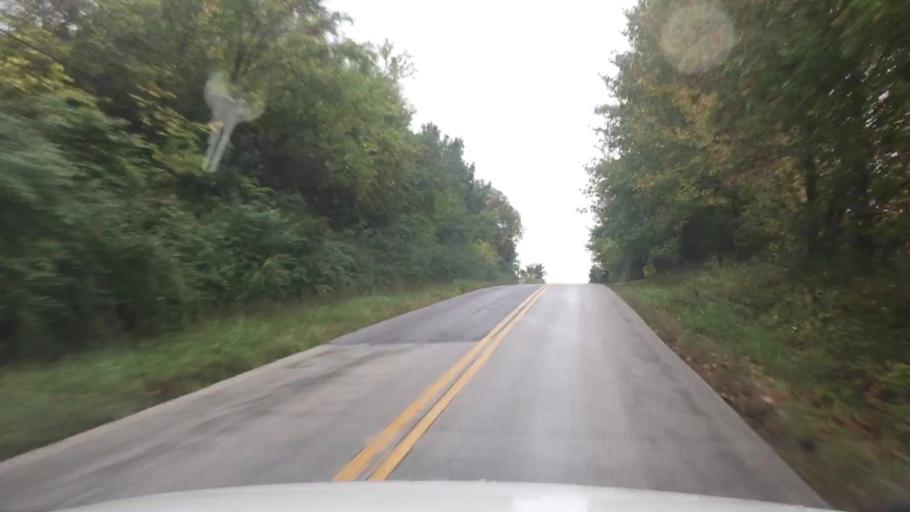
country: US
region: Missouri
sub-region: Boone County
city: Columbia
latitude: 38.9393
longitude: -92.4966
